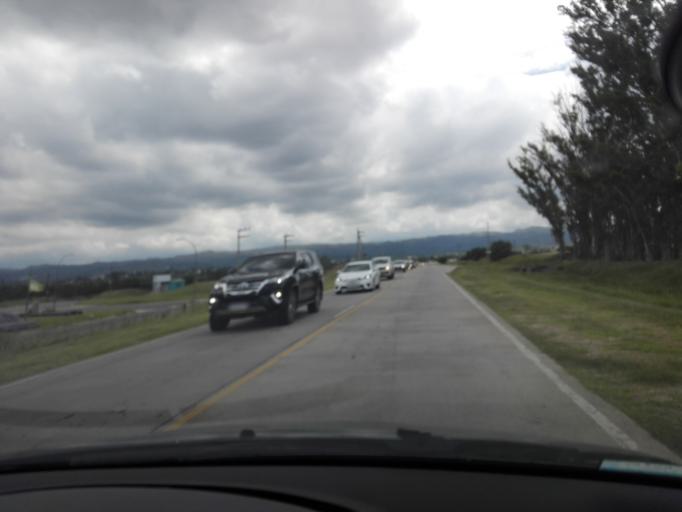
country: AR
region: Cordoba
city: Alta Gracia
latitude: -31.6347
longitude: -64.4231
